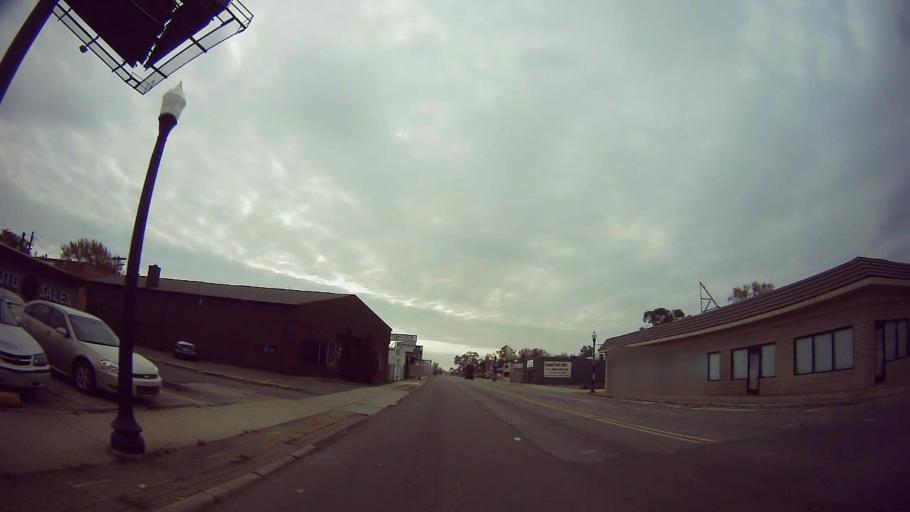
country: US
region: Michigan
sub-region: Oakland County
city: Hazel Park
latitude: 42.4584
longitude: -83.1037
